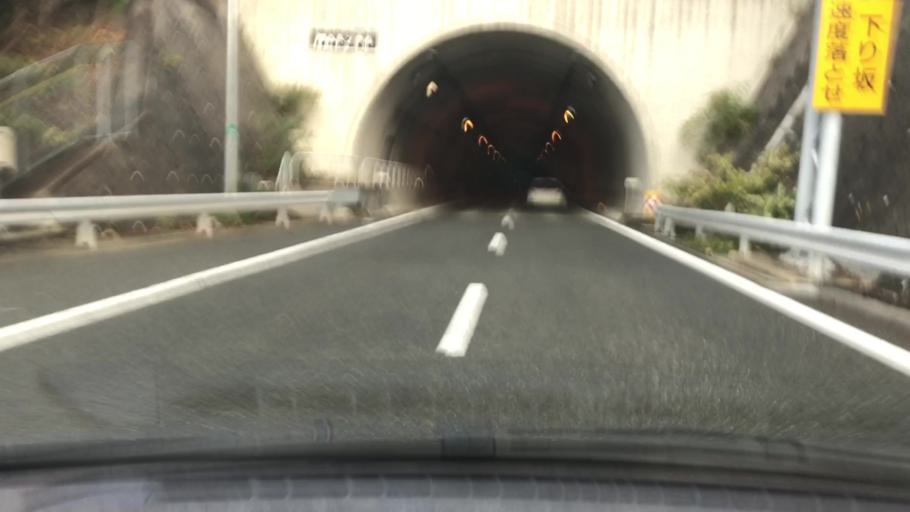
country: JP
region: Hyogo
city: Sandacho
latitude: 34.8243
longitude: 135.2602
